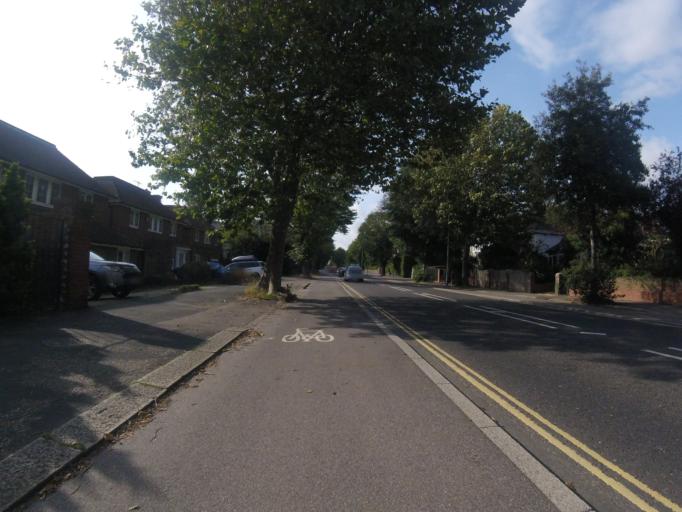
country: GB
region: England
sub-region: Brighton and Hove
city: Hove
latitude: 50.8370
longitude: -0.1647
